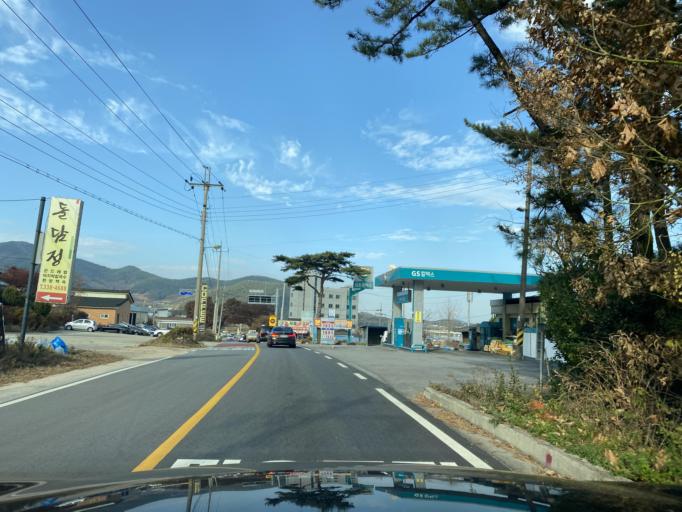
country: KR
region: Chungcheongnam-do
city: Hongsung
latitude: 36.6730
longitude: 126.6425
